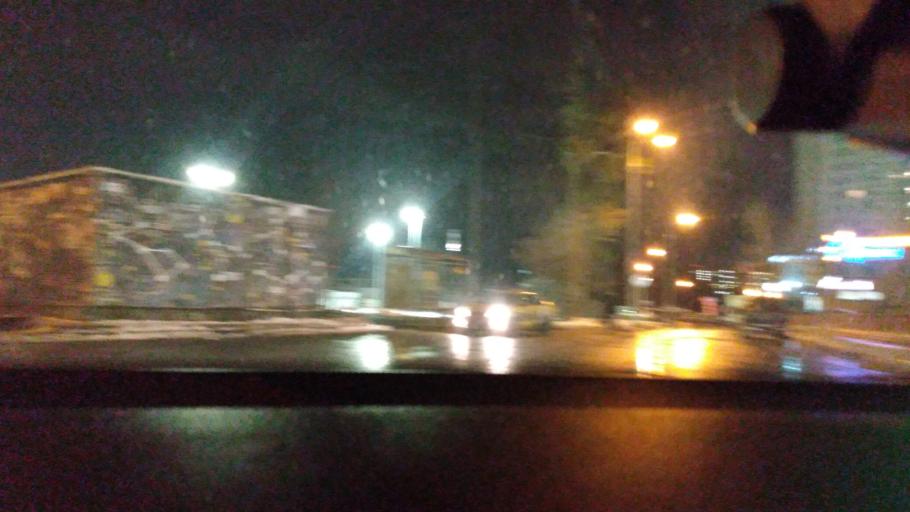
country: RU
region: Moskovskaya
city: Zheleznodorozhnyy
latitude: 55.7469
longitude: 37.9862
